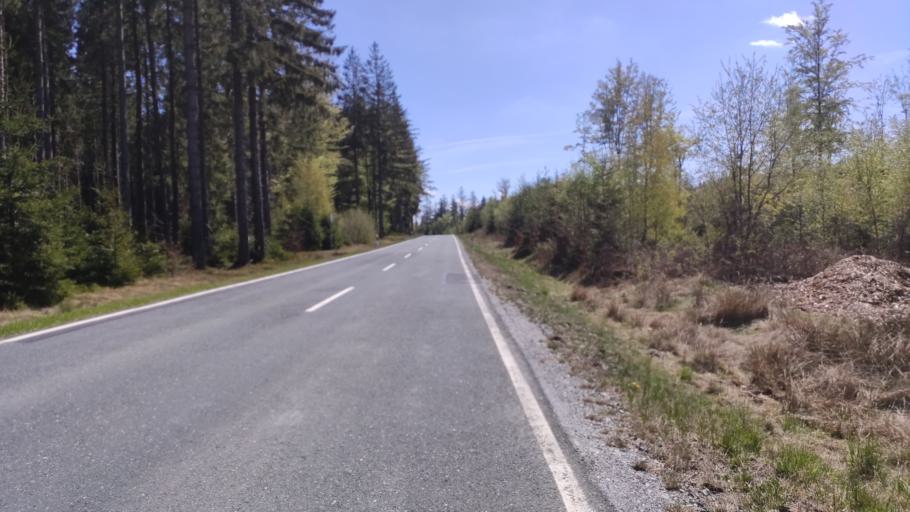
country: DE
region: Bavaria
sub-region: Upper Franconia
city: Tschirn
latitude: 50.3679
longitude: 11.4544
